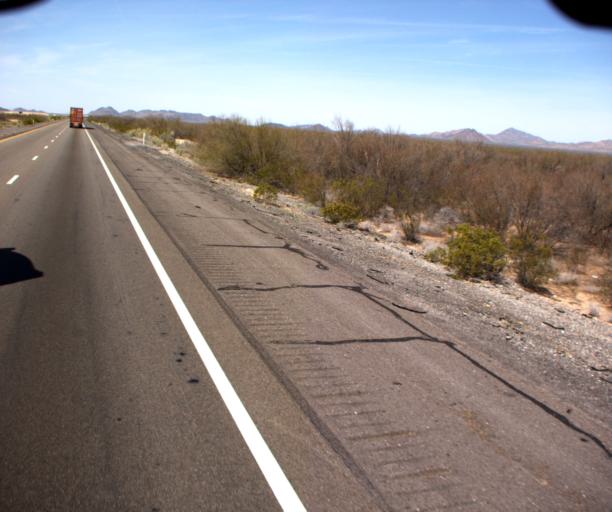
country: US
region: Arizona
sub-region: La Paz County
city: Salome
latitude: 33.5925
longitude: -113.5071
